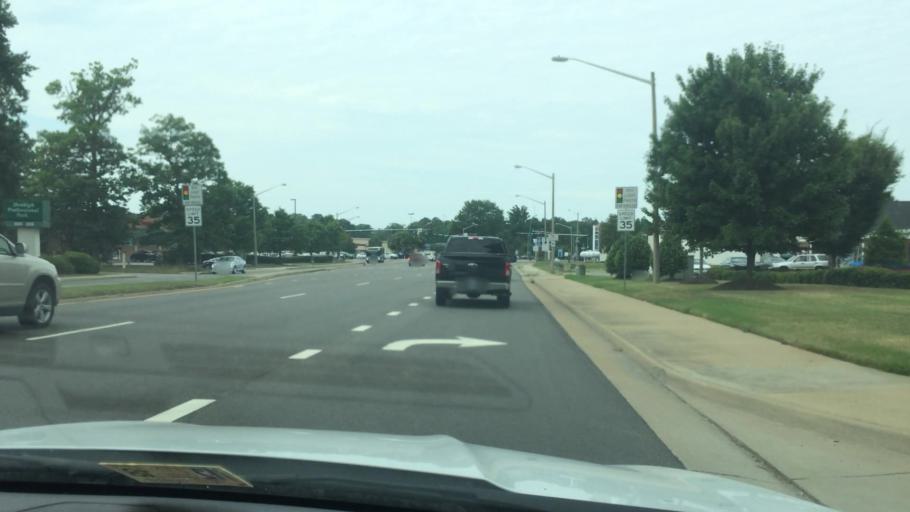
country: US
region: Virginia
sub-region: York County
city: Yorktown
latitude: 37.1399
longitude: -76.5189
